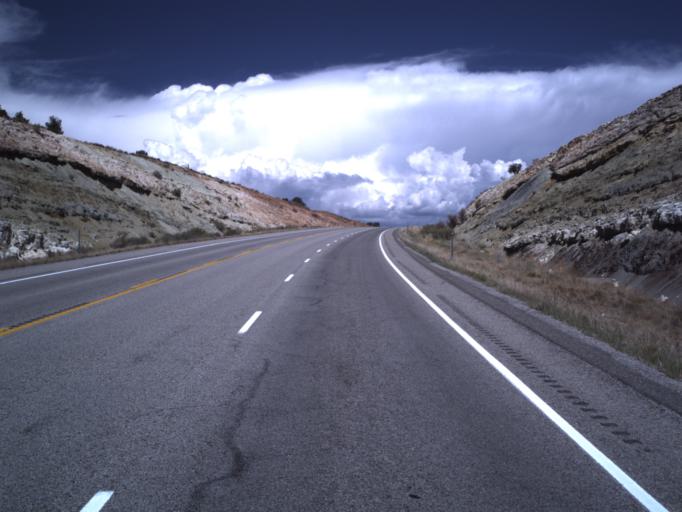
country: US
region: Utah
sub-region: San Juan County
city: Blanding
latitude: 37.4329
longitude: -109.4714
